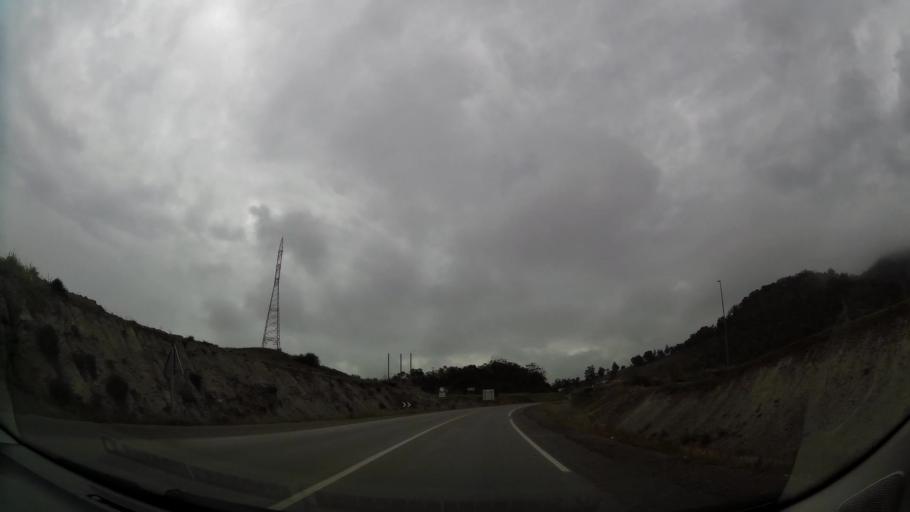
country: MA
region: Oriental
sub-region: Nador
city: Nador
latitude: 35.1500
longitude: -3.0198
